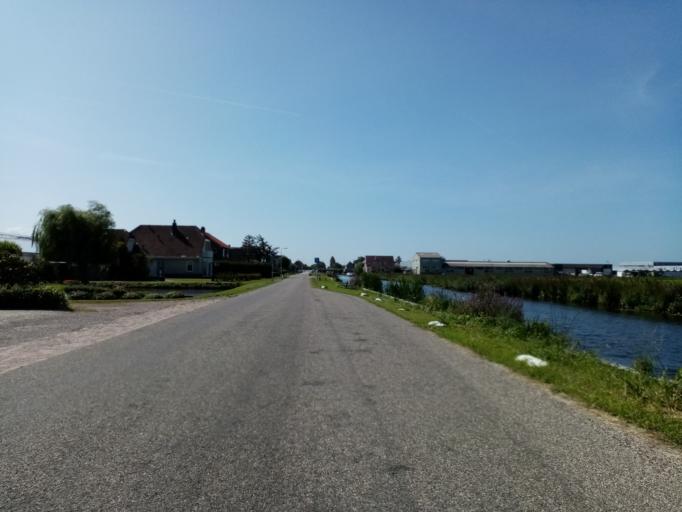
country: NL
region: South Holland
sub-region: Gemeente Hillegom
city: Hillegom
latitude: 52.3010
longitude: 4.5571
